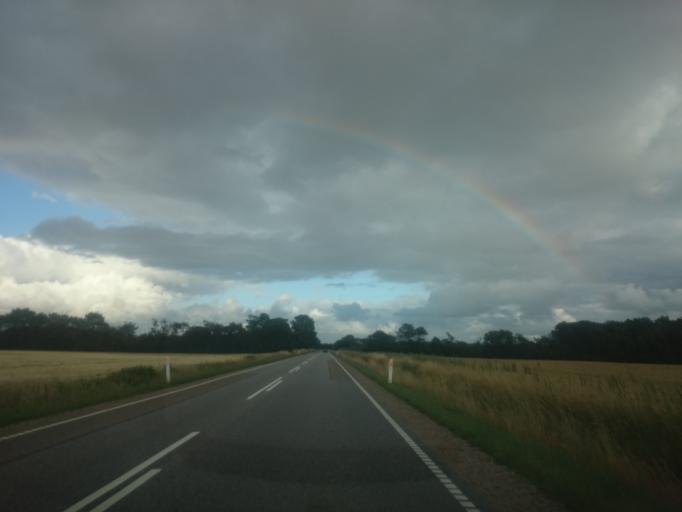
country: DK
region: South Denmark
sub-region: Billund Kommune
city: Grindsted
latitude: 55.6589
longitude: 8.7846
